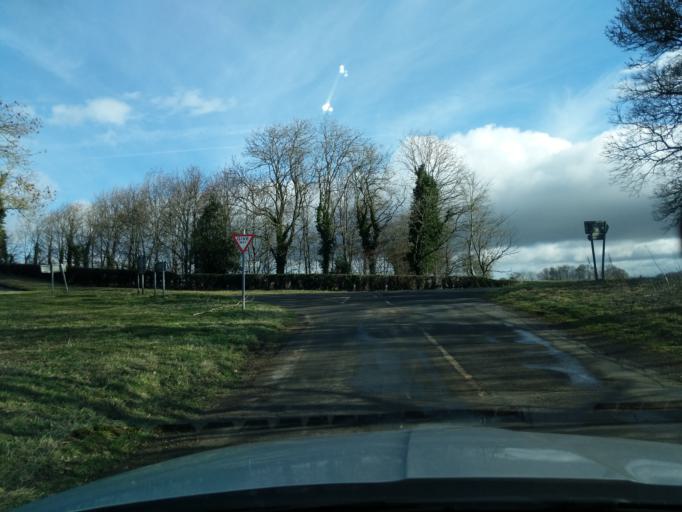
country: GB
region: England
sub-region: North Yorkshire
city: Catterick Garrison
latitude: 54.3417
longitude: -1.6915
